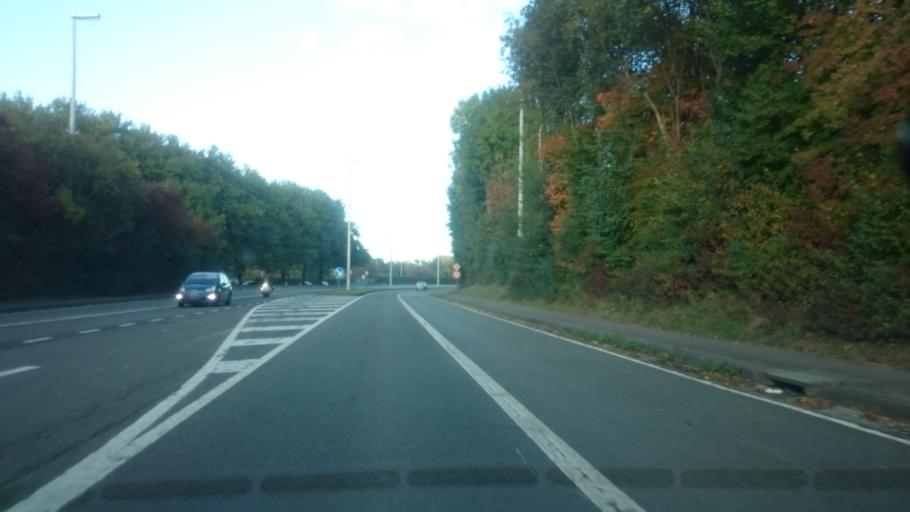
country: BE
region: Wallonia
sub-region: Province du Brabant Wallon
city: Louvain-la-Neuve
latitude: 50.6688
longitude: 4.5954
